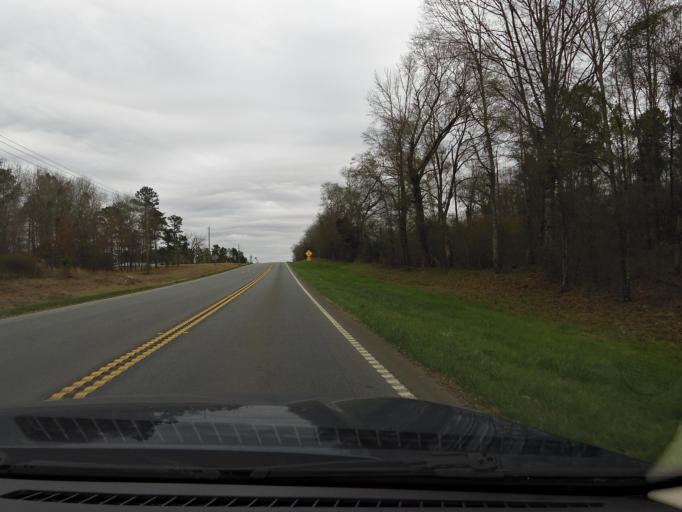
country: US
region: Georgia
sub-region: Randolph County
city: Cuthbert
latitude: 31.7757
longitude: -84.7439
